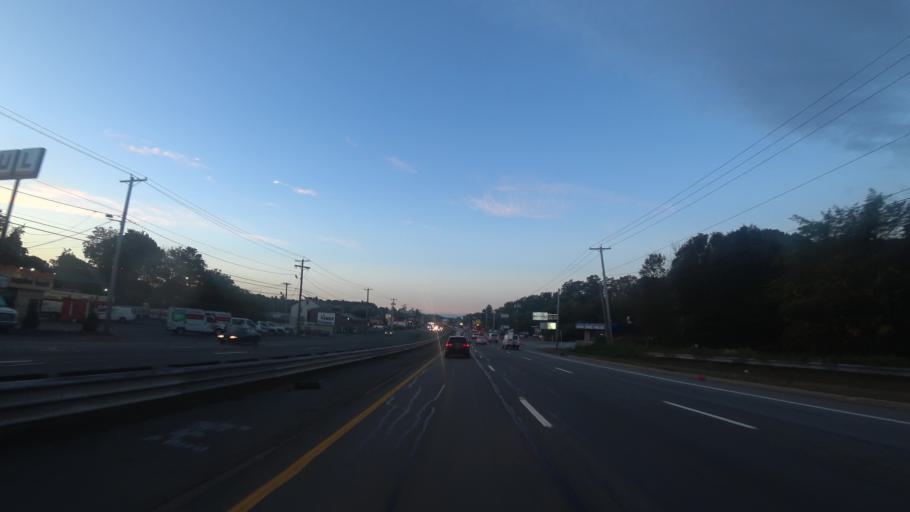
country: US
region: Massachusetts
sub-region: Essex County
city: Saugus
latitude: 42.4986
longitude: -71.0154
